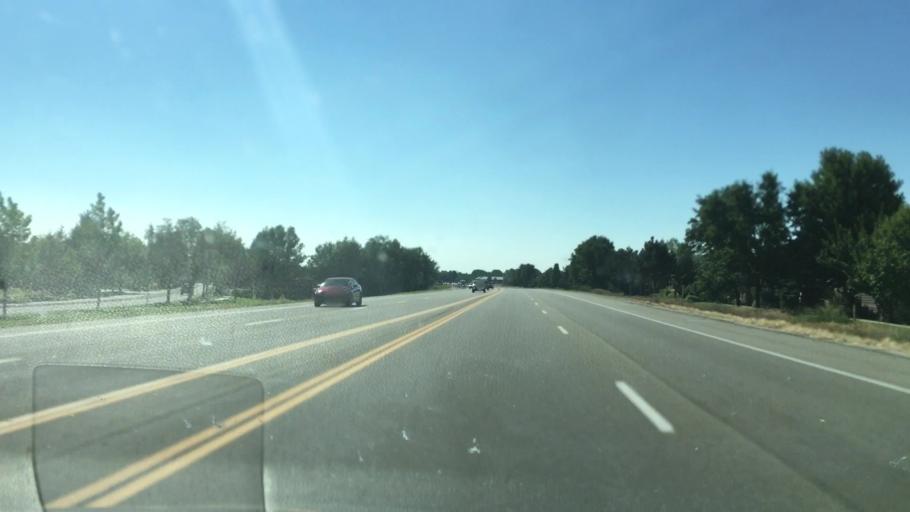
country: US
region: Idaho
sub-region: Ada County
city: Eagle
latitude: 43.6887
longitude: -116.3373
